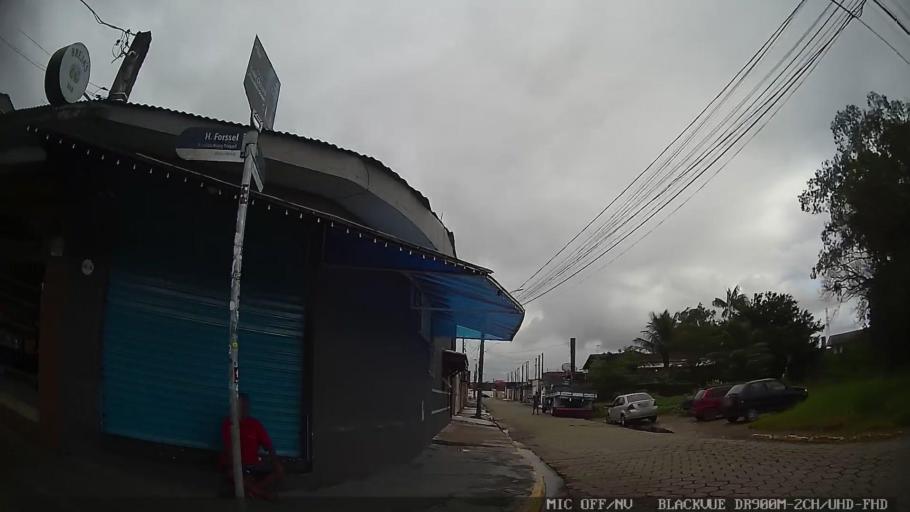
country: BR
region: Sao Paulo
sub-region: Itanhaem
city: Itanhaem
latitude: -24.1865
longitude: -46.8169
